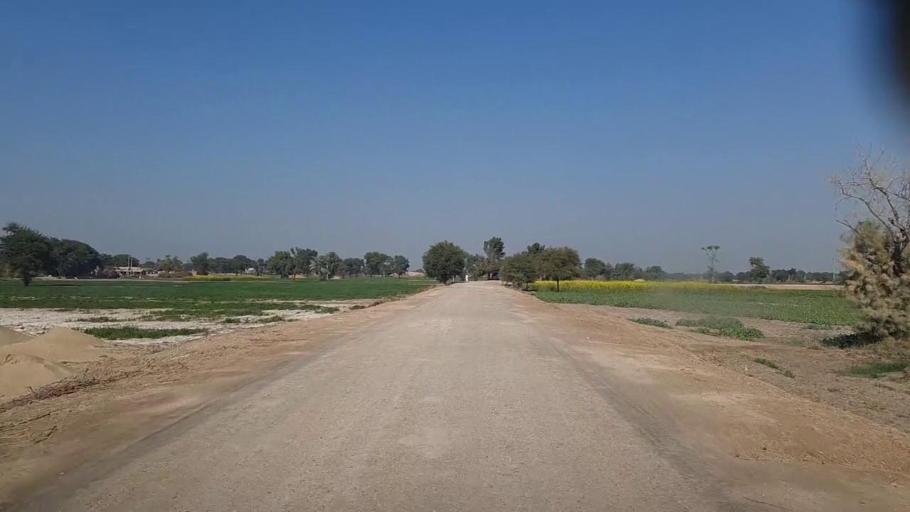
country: PK
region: Sindh
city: Khairpur
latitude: 27.9937
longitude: 69.8476
